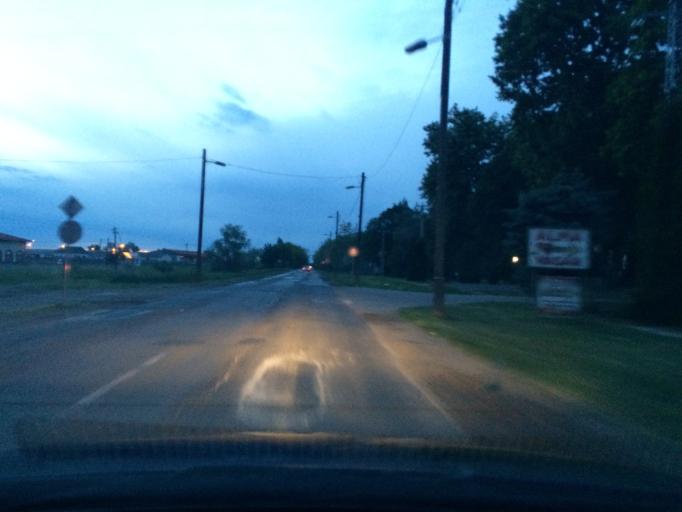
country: HU
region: Hajdu-Bihar
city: Hajdunanas
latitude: 47.9063
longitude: 21.4036
